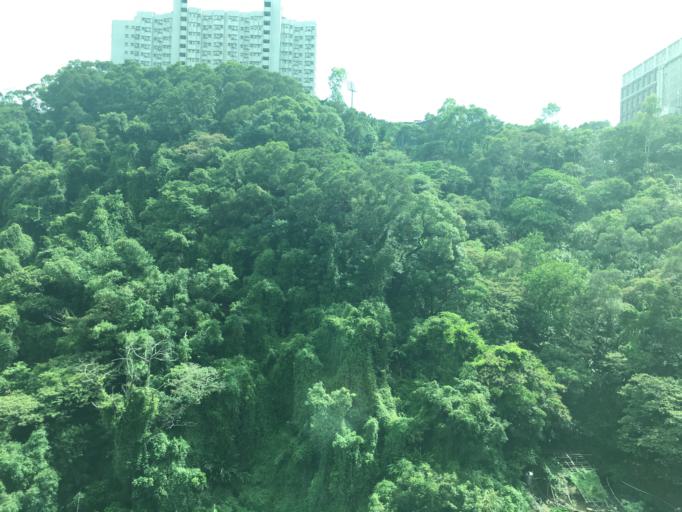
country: TW
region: Taipei
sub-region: Taipei
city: Banqiao
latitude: 25.0345
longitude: 121.3933
